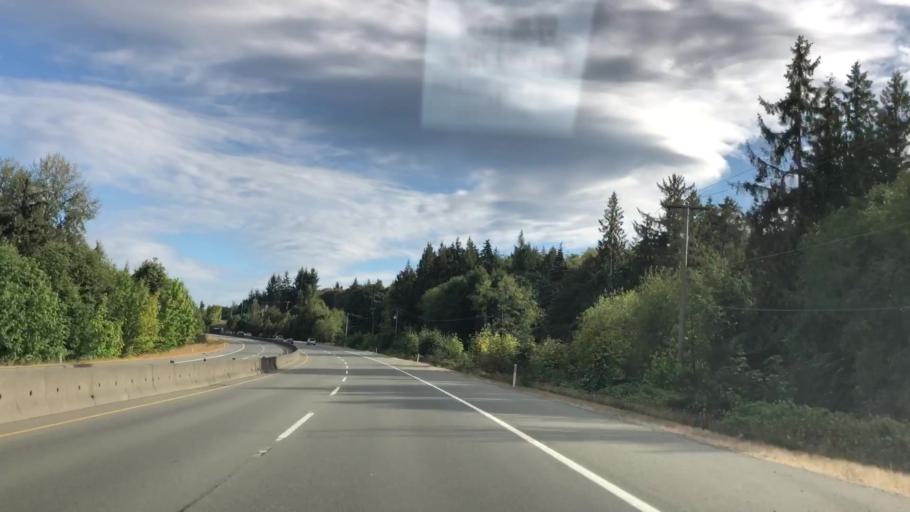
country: CA
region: British Columbia
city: North Saanich
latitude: 48.6500
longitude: -123.5597
